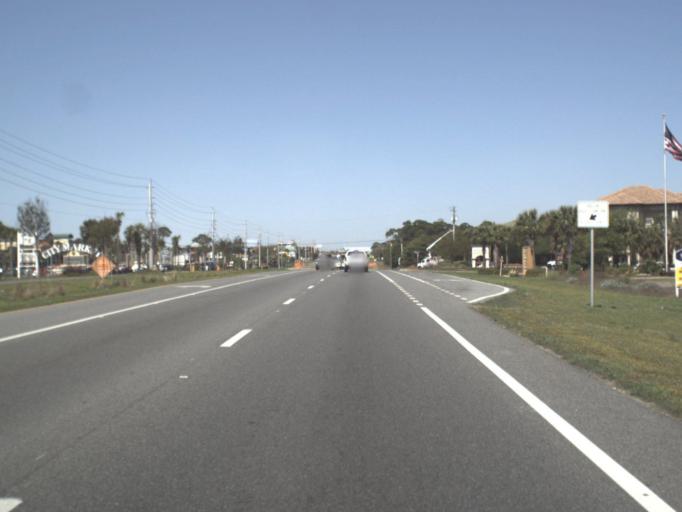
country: US
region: Florida
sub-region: Walton County
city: Miramar Beach
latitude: 30.3869
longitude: -86.4046
